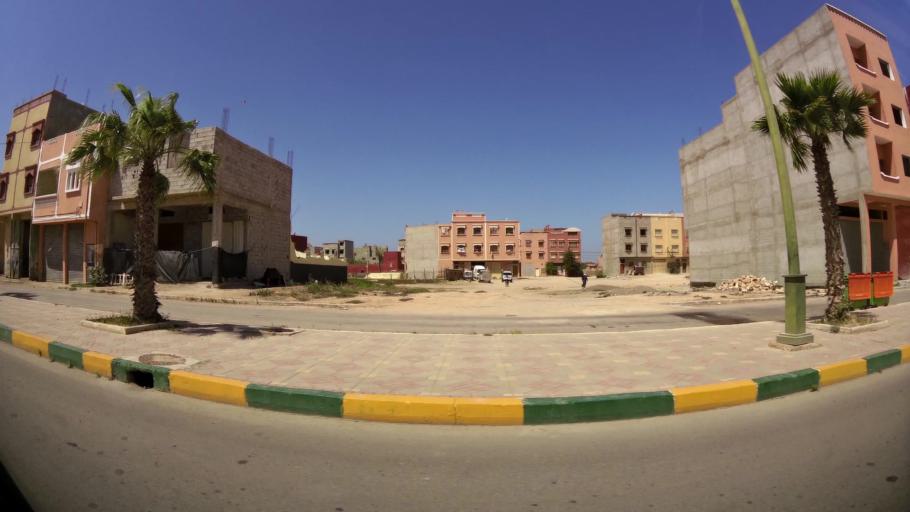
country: MA
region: Souss-Massa-Draa
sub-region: Inezgane-Ait Mellou
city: Inezgane
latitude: 30.3156
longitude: -9.5030
